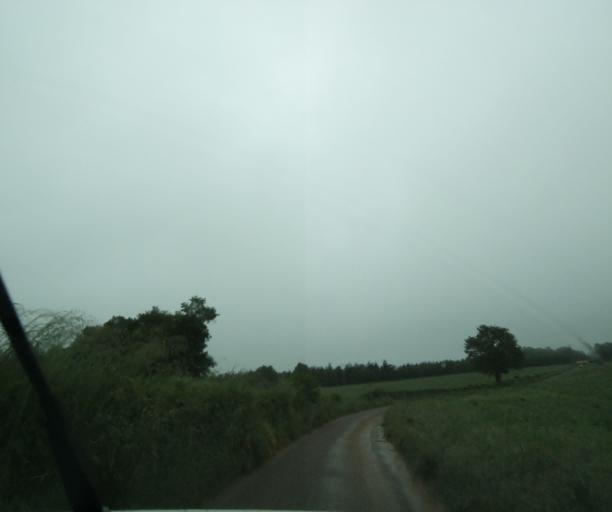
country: FR
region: Bourgogne
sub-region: Departement de Saone-et-Loire
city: Charolles
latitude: 46.3908
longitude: 4.3669
